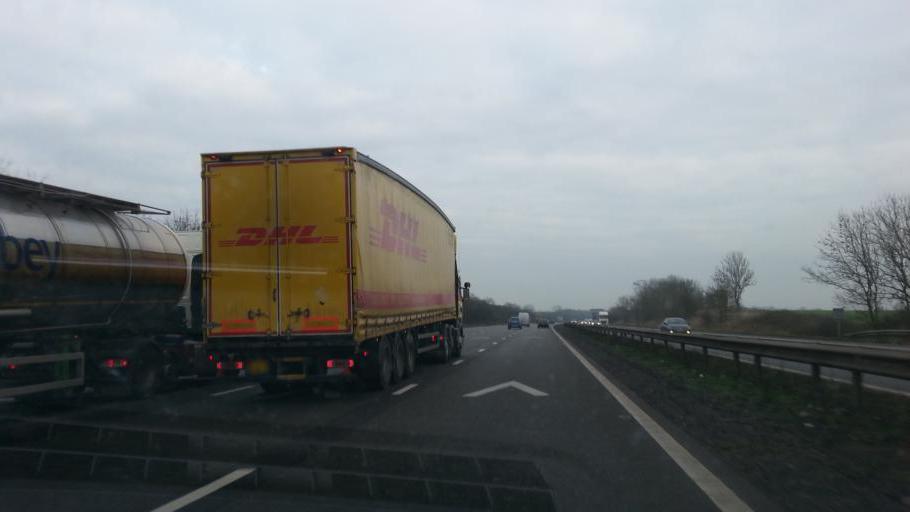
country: GB
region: England
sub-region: Warwickshire
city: Brandon
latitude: 52.4351
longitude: -1.3576
